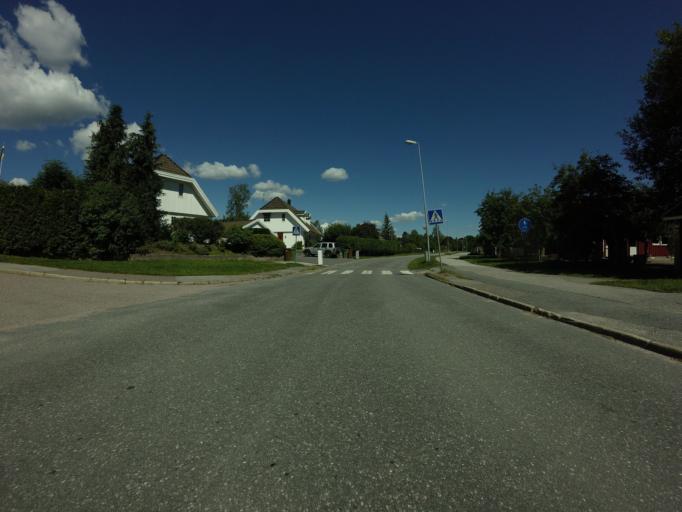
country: SE
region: Stockholm
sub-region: Sollentuna Kommun
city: Sollentuna
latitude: 59.4549
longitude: 17.9014
